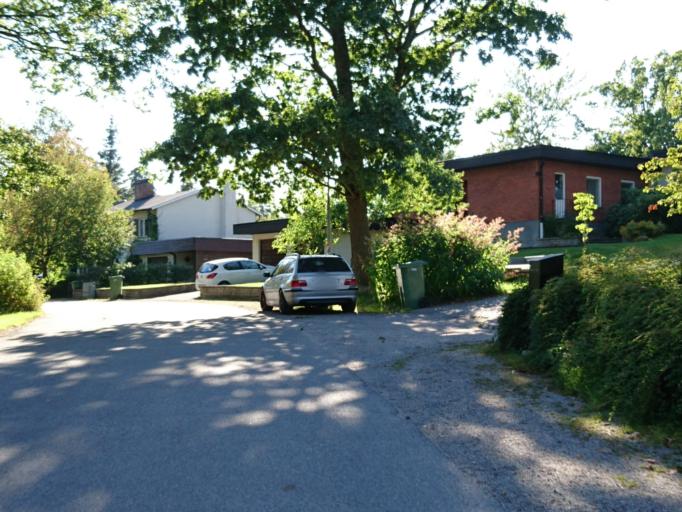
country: SE
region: Stockholm
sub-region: Huddinge Kommun
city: Segeltorp
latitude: 59.2648
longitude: 17.9618
